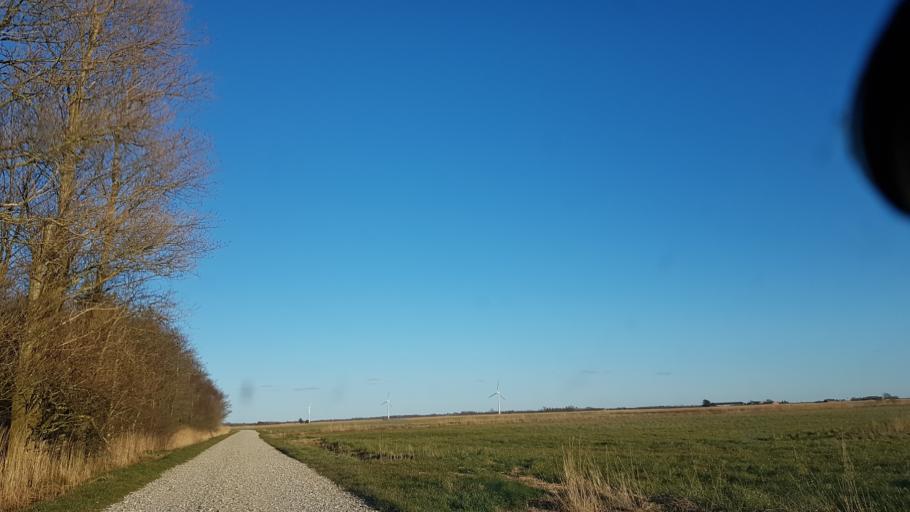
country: DK
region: South Denmark
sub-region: Esbjerg Kommune
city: Bramming
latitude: 55.4150
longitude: 8.6543
